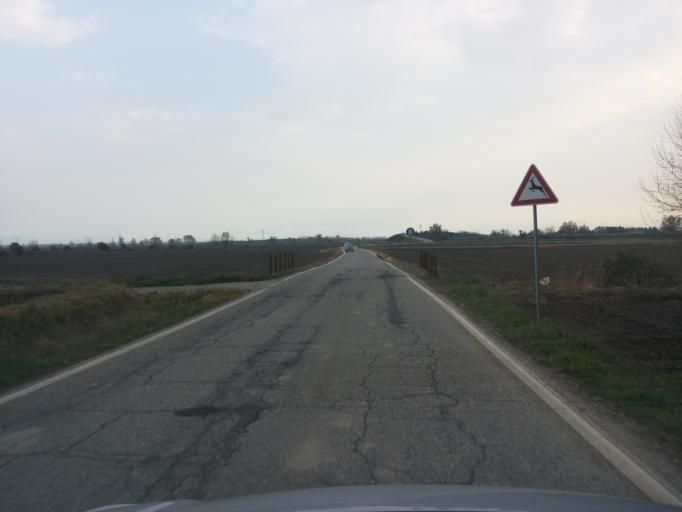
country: IT
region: Piedmont
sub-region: Provincia di Vercelli
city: Caresana
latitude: 45.1985
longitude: 8.4963
